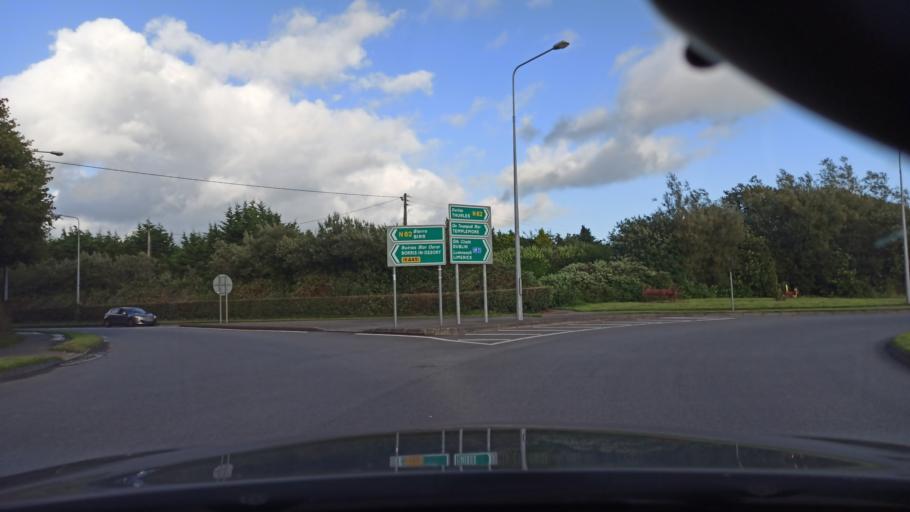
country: IE
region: Munster
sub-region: North Tipperary
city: Roscrea
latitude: 52.9473
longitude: -7.7960
